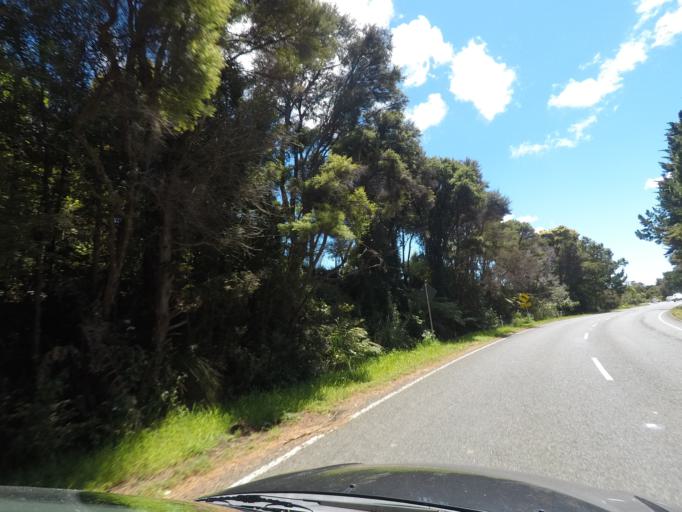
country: NZ
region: Auckland
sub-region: Auckland
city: Rothesay Bay
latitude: -36.7383
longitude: 174.6751
